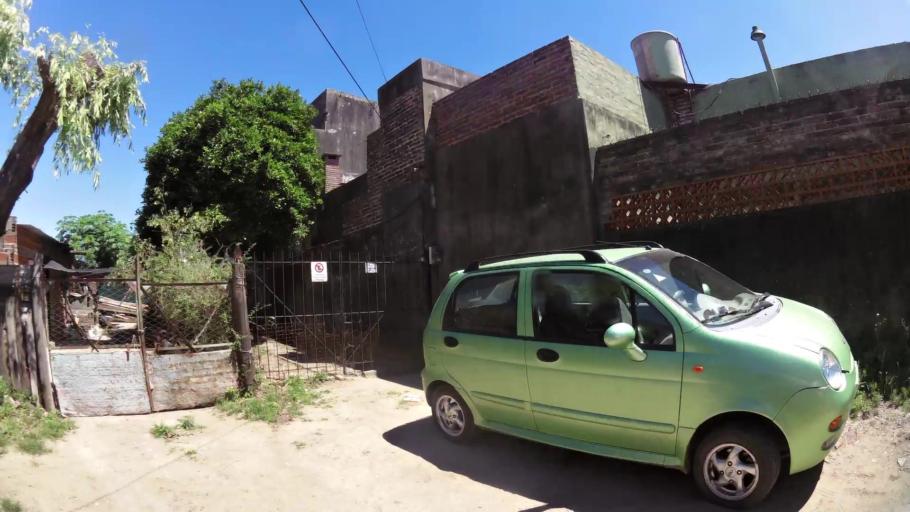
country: AR
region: Santa Fe
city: Santa Fe de la Vera Cruz
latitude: -31.6263
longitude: -60.7169
